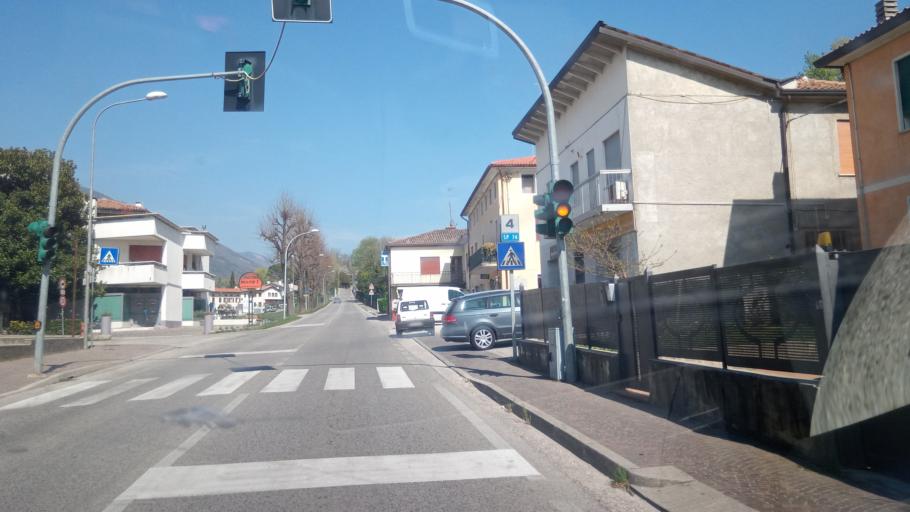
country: IT
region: Veneto
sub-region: Provincia di Treviso
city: Borso del Grappa
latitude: 45.7976
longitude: 11.7605
